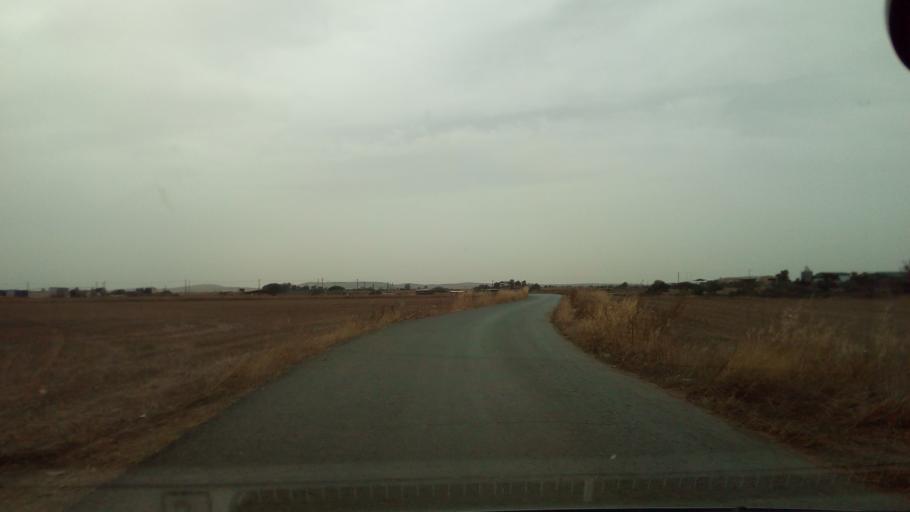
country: CY
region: Larnaka
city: Xylotymbou
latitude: 35.0174
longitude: 33.7339
